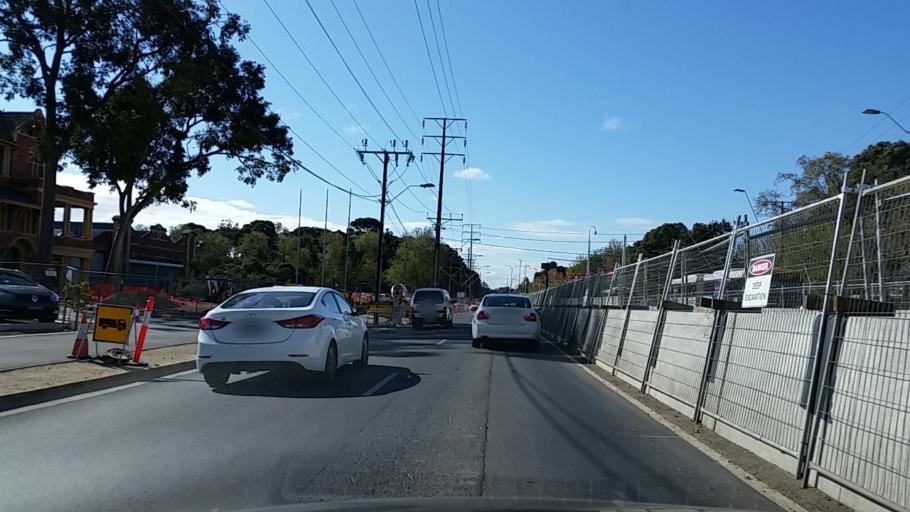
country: AU
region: South Australia
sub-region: Adelaide
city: Adelaide
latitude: -34.9181
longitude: 138.6147
